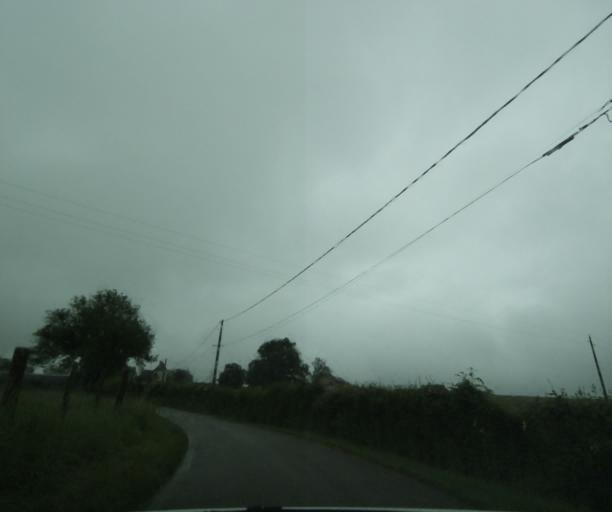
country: FR
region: Bourgogne
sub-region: Departement de Saone-et-Loire
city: Charolles
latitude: 46.4546
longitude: 4.2091
